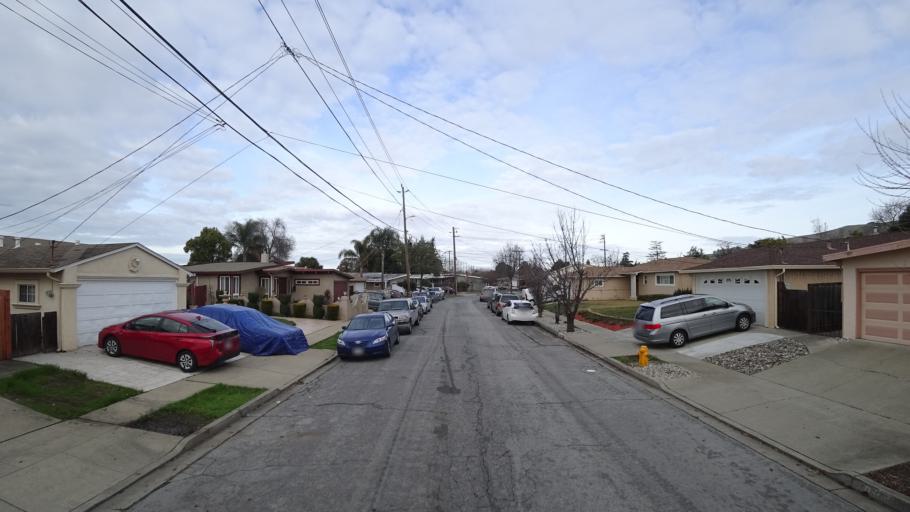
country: US
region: California
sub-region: Alameda County
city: Union City
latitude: 37.6194
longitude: -122.0453
